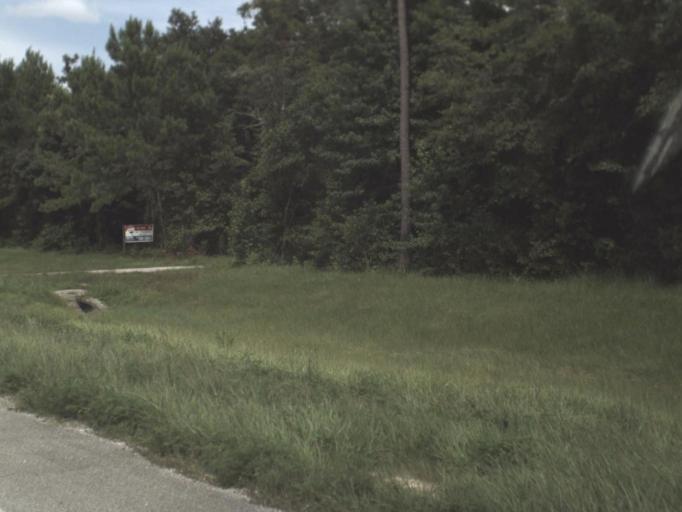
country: US
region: Florida
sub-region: Hernando County
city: South Brooksville
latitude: 28.4879
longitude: -82.4312
